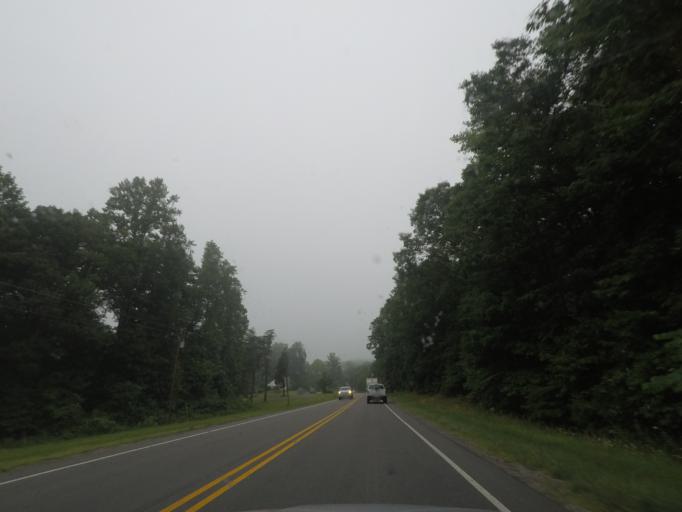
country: US
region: Virginia
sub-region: Buckingham County
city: Buckingham
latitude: 37.4741
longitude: -78.4709
